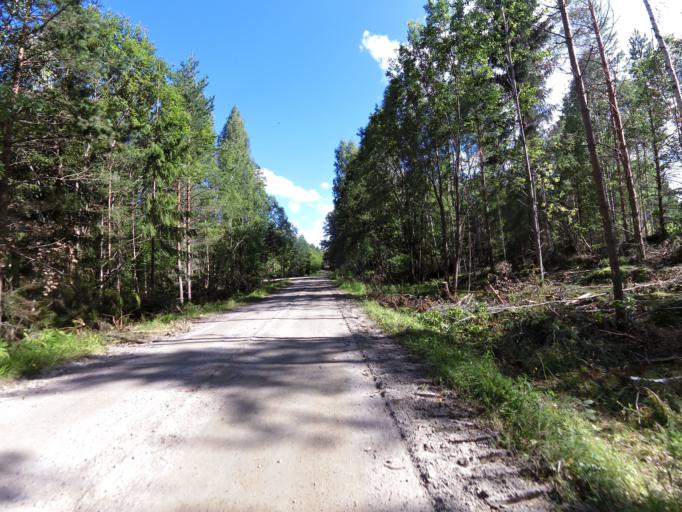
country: SE
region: Gaevleborg
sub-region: Hofors Kommun
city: Hofors
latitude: 60.5046
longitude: 16.3631
